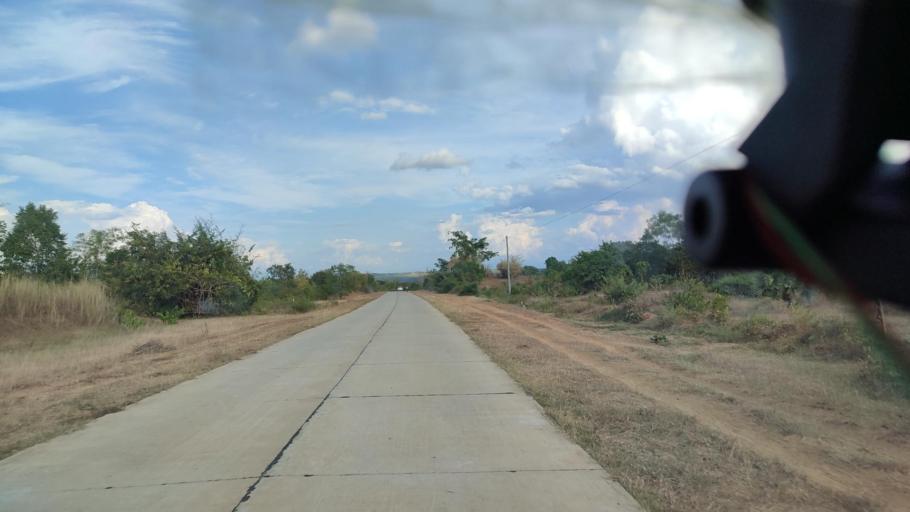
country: MM
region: Mandalay
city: Yamethin
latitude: 20.0968
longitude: 95.9759
